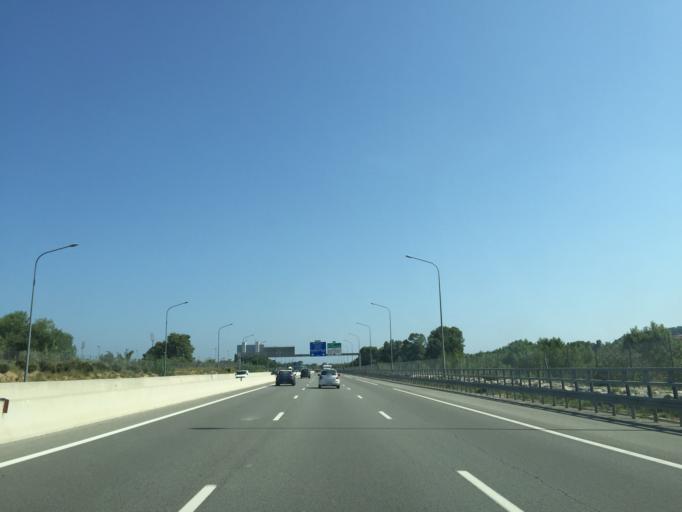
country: FR
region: Provence-Alpes-Cote d'Azur
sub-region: Departement des Alpes-Maritimes
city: Saint-Laurent-du-Var
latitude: 43.6843
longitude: 7.1916
